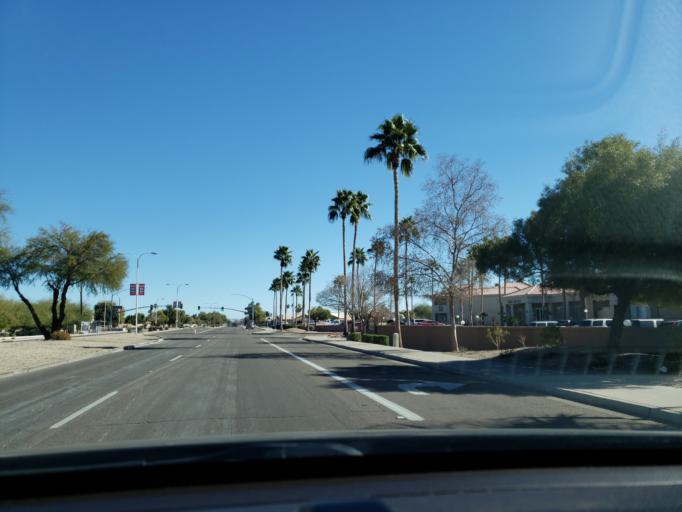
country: US
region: Arizona
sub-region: Maricopa County
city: Chandler
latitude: 33.3206
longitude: -111.8346
